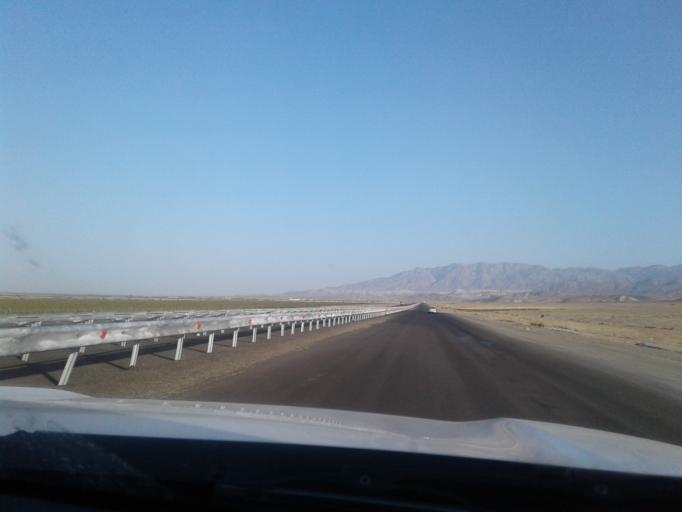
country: TM
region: Ahal
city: Baharly
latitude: 38.6749
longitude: 56.8601
